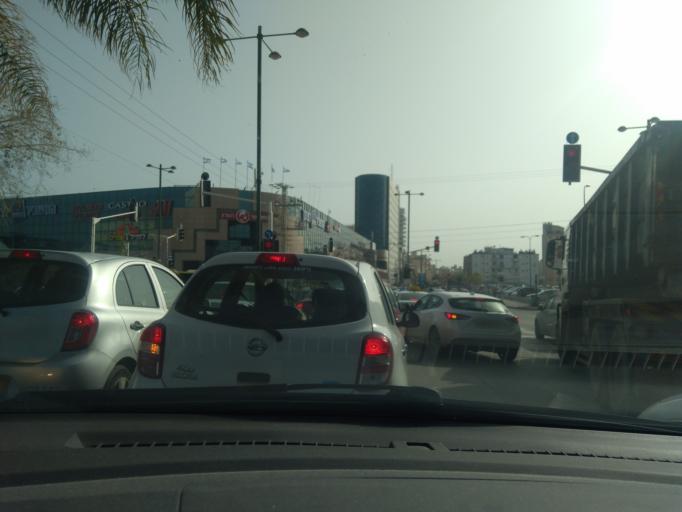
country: IL
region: Central District
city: Netanya
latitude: 32.3274
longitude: 34.8615
